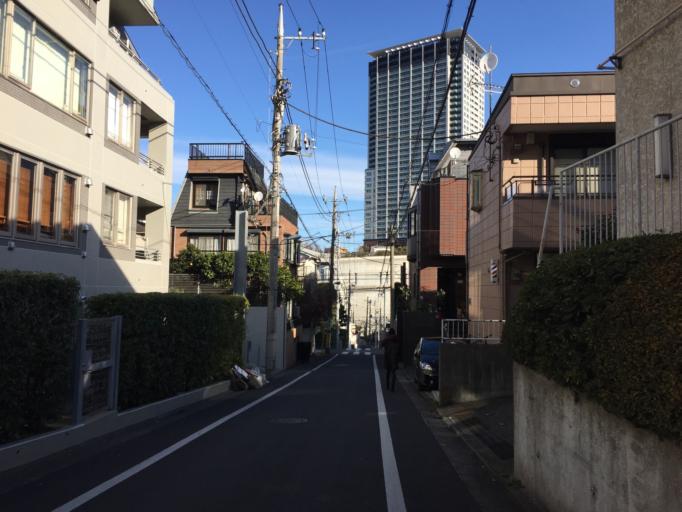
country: JP
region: Tokyo
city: Tokyo
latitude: 35.6487
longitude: 139.6869
